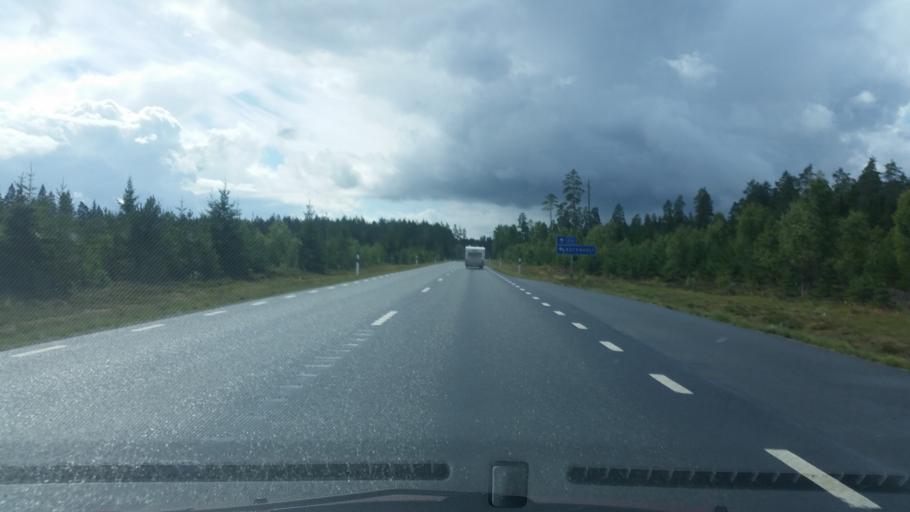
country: SE
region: Joenkoeping
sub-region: Gislaveds Kommun
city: Gislaved
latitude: 57.3663
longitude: 13.5706
